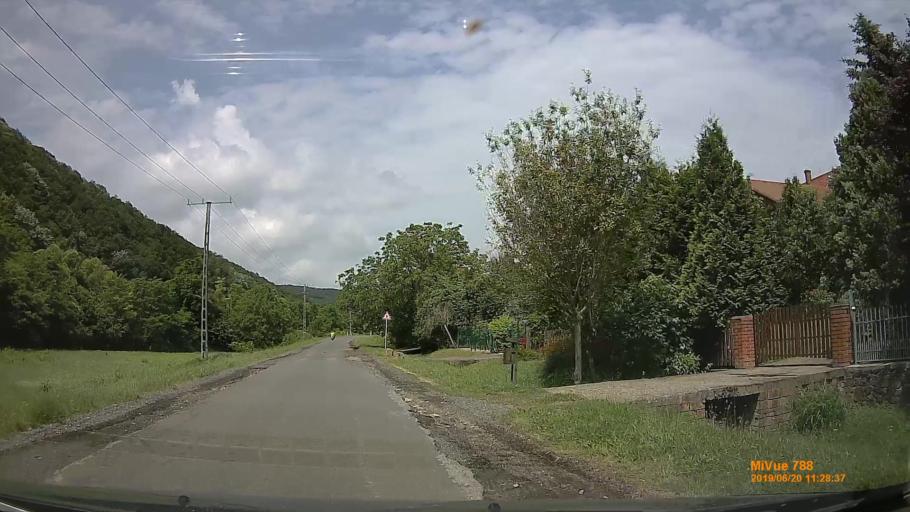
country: HU
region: Baranya
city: Mecseknadasd
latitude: 46.2235
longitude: 18.4482
